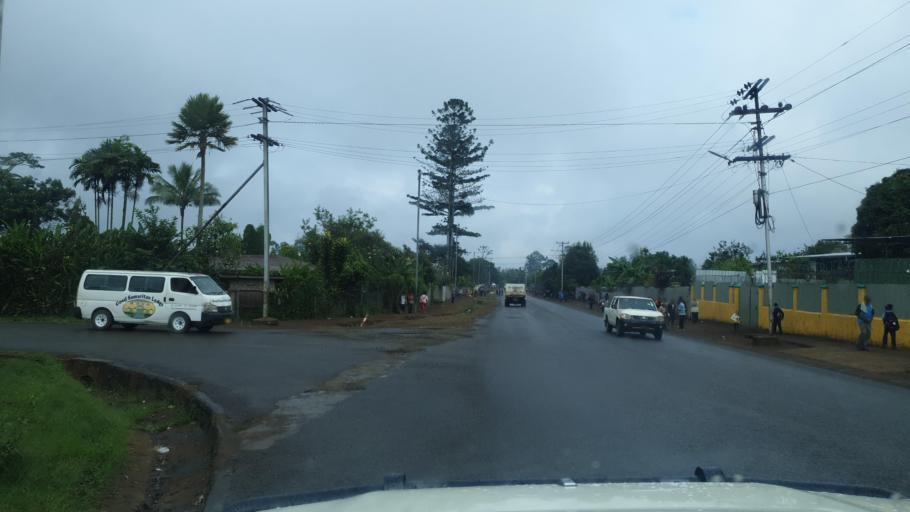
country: PG
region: Eastern Highlands
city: Goroka
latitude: -6.0775
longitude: 145.3875
